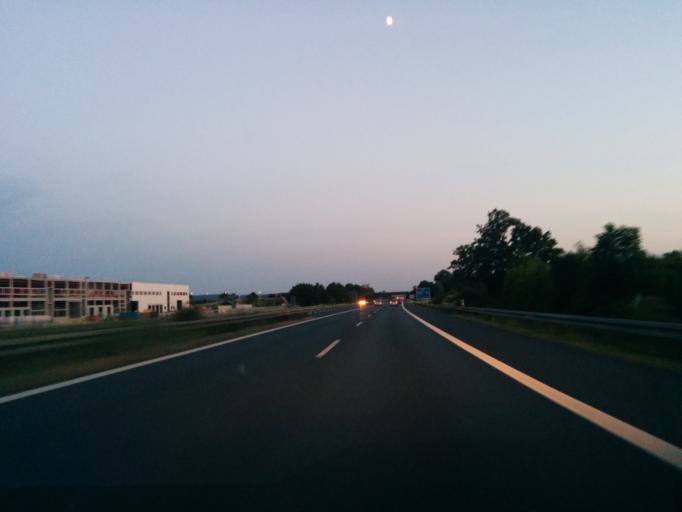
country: DE
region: Bavaria
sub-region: Upper Franconia
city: Forchheim
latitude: 49.6907
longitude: 11.0599
